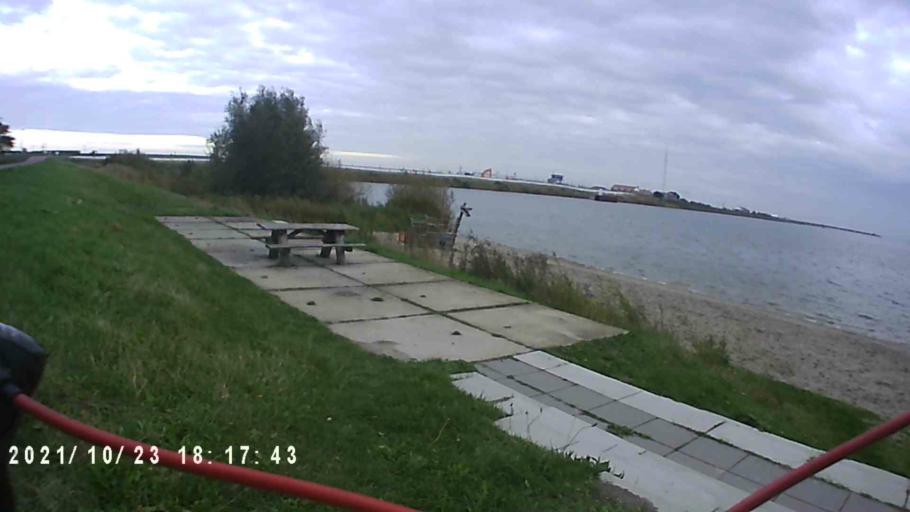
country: NL
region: North Holland
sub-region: Gemeente Hollands Kroon
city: Den Oever
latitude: 52.9318
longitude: 5.0394
